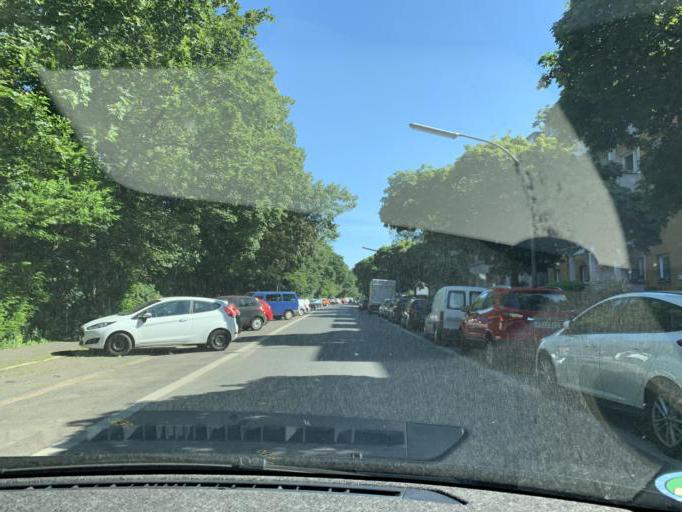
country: DE
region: North Rhine-Westphalia
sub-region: Regierungsbezirk Koln
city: Nippes
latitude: 50.9802
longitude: 6.9515
